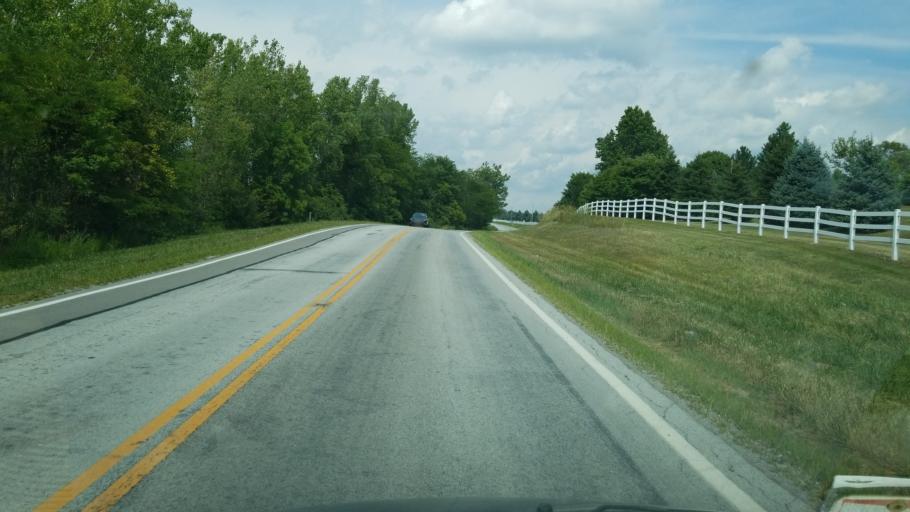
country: US
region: Ohio
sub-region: Hancock County
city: Arlington
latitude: 40.9149
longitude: -83.5563
